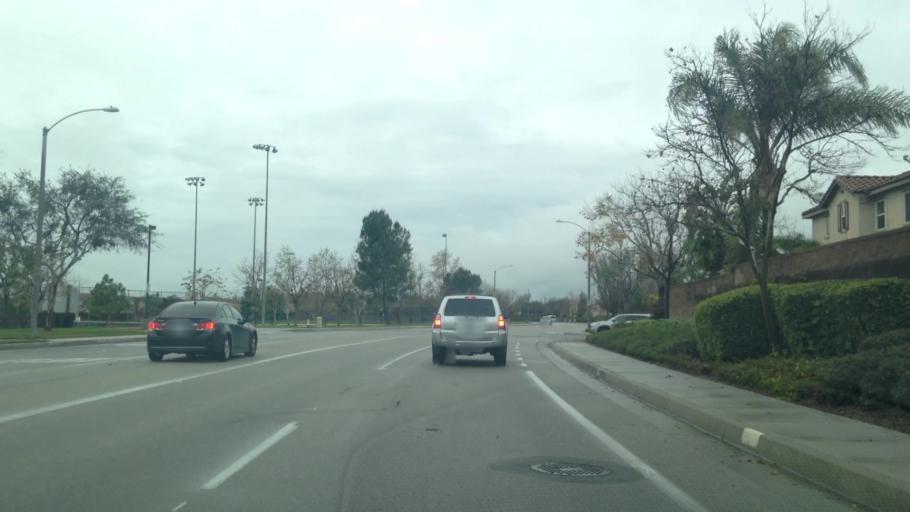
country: US
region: California
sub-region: Riverside County
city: Norco
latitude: 33.9673
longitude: -117.5681
